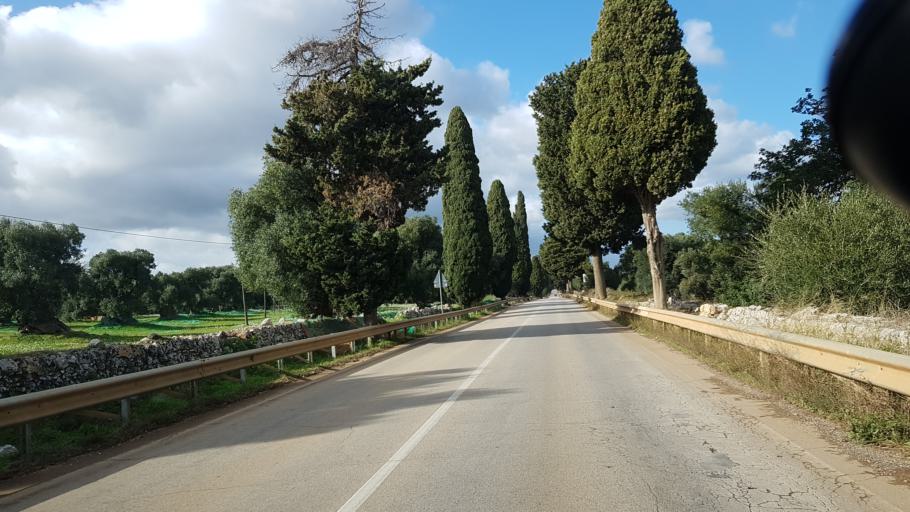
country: IT
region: Apulia
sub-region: Provincia di Brindisi
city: Ostuni
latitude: 40.7521
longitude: 17.5476
